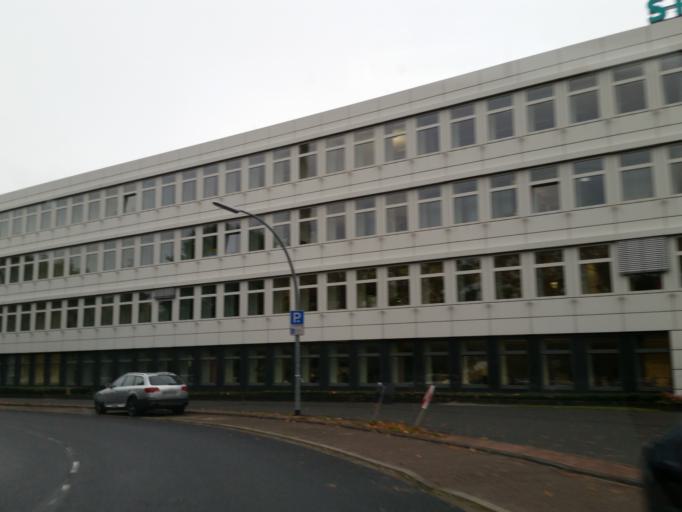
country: DE
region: Lower Saxony
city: Braunschweig
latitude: 52.2501
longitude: 10.5435
